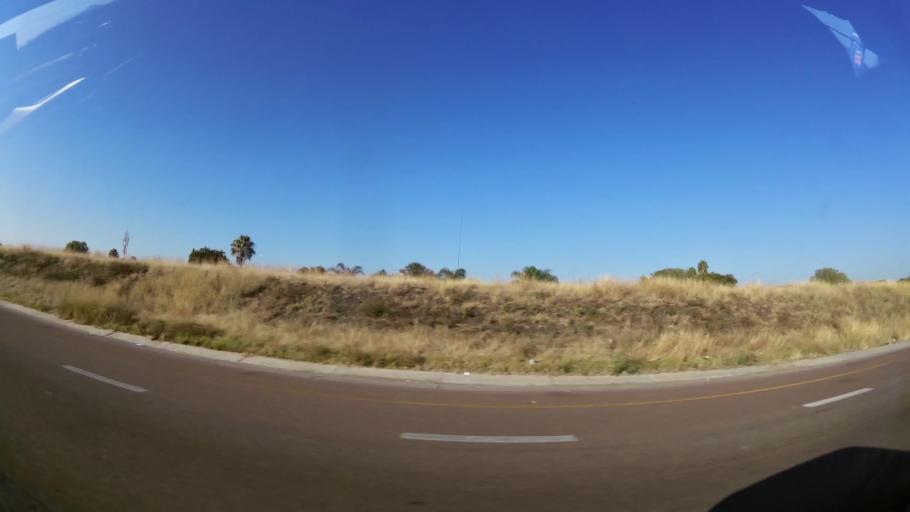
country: ZA
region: Gauteng
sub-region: City of Tshwane Metropolitan Municipality
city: Pretoria
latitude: -25.6434
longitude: 28.2426
